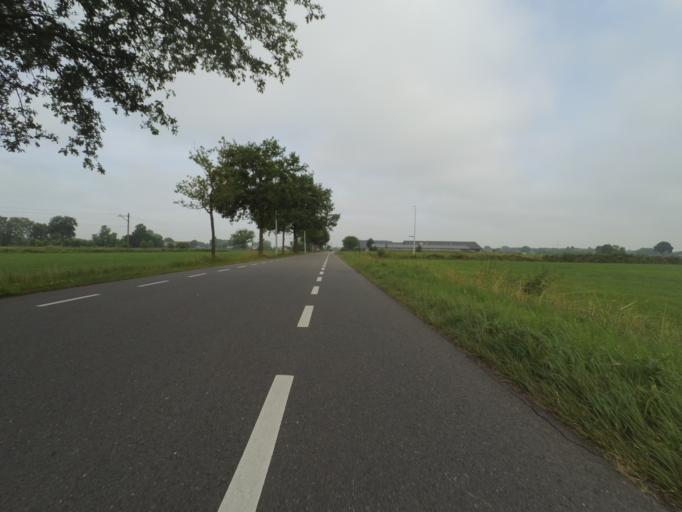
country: NL
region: Gelderland
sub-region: Gemeente Barneveld
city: Barneveld
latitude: 52.1211
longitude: 5.6139
